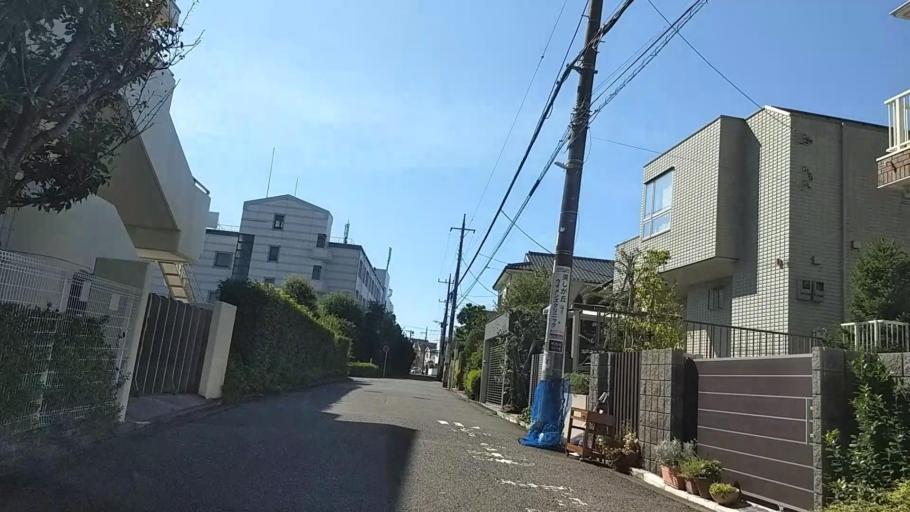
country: JP
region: Tokyo
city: Chofugaoka
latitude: 35.5754
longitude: 139.5602
